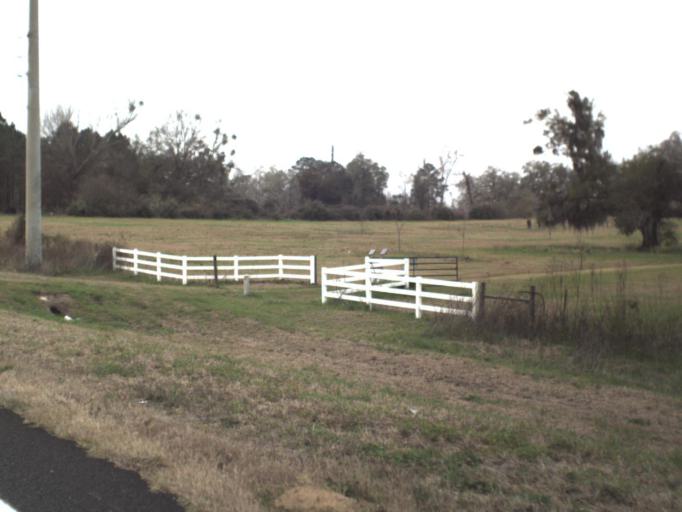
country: US
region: Florida
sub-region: Jefferson County
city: Monticello
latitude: 30.4120
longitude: -83.9478
